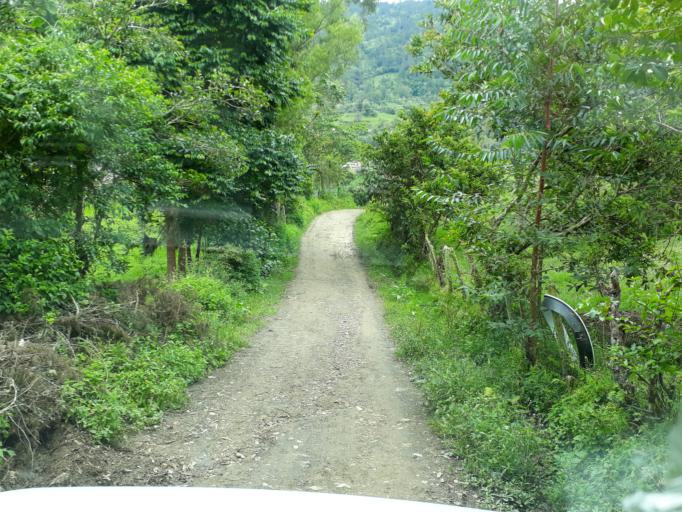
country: CO
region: Cundinamarca
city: Gacheta
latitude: 4.8120
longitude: -73.6421
